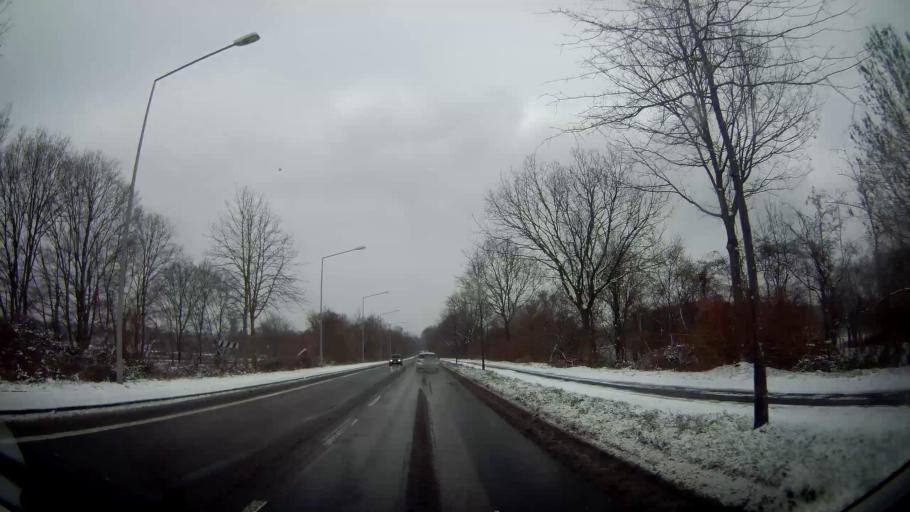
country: DE
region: North Rhine-Westphalia
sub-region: Regierungsbezirk Munster
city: Gladbeck
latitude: 51.5835
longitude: 6.9878
